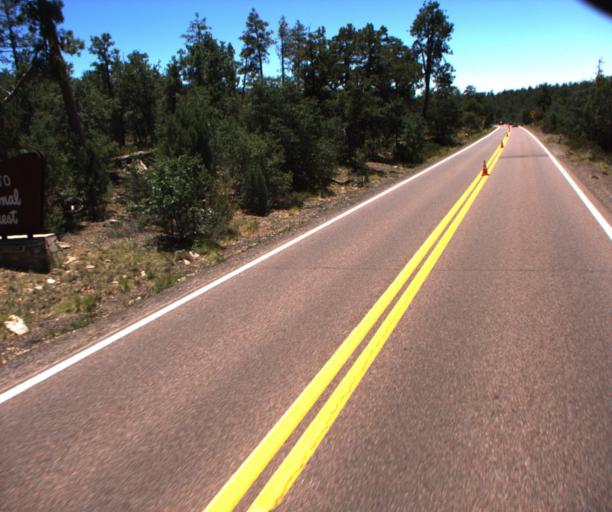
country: US
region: Arizona
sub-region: Gila County
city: Pine
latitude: 34.4258
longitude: -111.5108
